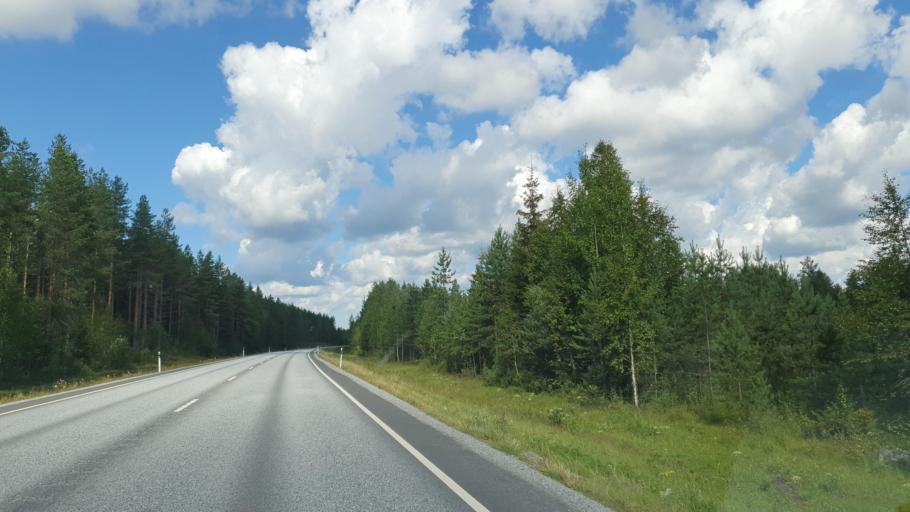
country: FI
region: Northern Savo
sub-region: Ylae-Savo
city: Sonkajaervi
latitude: 63.9051
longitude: 27.3905
